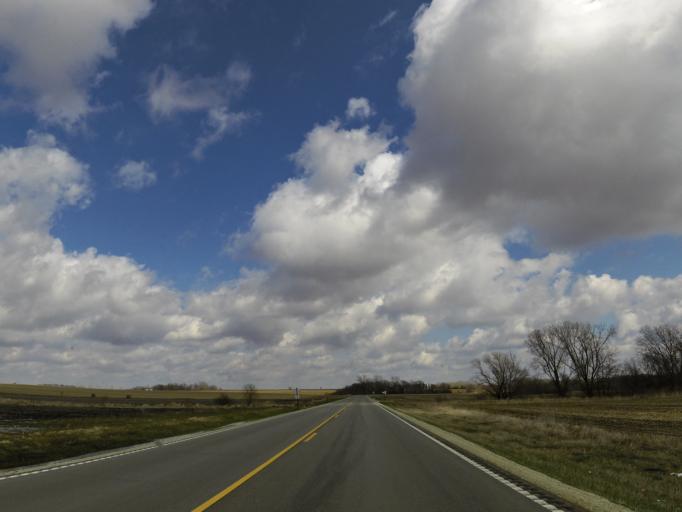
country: US
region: Minnesota
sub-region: Dodge County
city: Dodge Center
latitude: 44.0841
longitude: -92.8372
